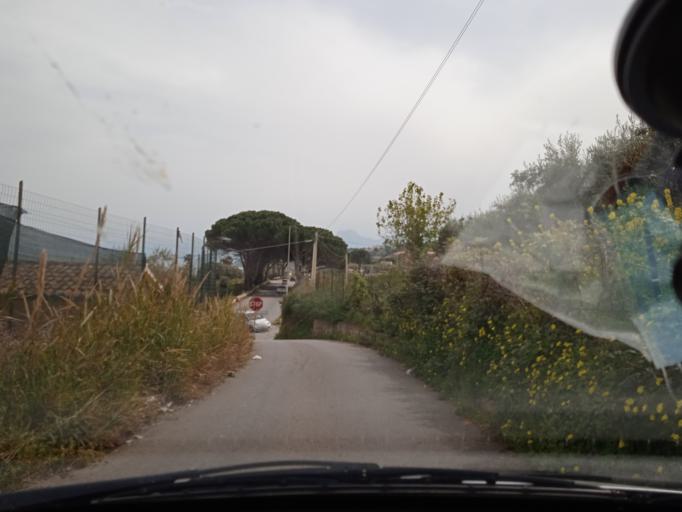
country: IT
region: Sicily
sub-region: Palermo
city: Altavilla Milicia
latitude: 38.0405
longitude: 13.5622
